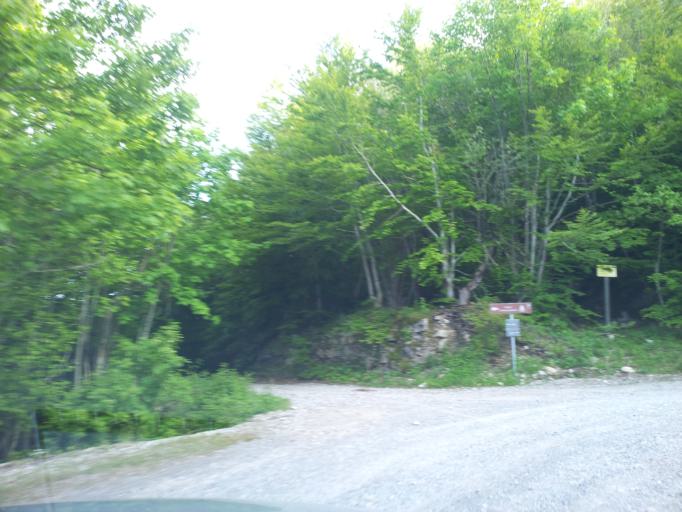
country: HR
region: Zadarska
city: Obrovac
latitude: 44.2962
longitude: 15.6678
